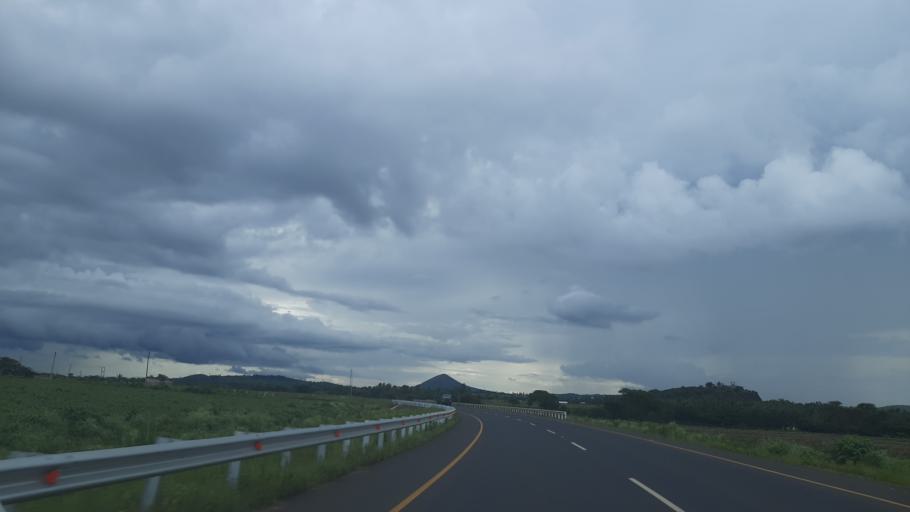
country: TZ
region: Arusha
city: Arusha
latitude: -3.3722
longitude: 36.6108
